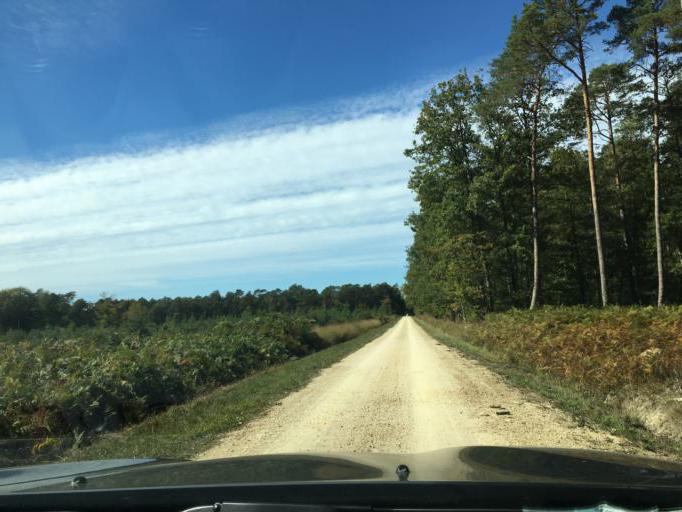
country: FR
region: Centre
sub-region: Departement d'Indre-et-Loire
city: Cheille
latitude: 47.2251
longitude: 0.4156
